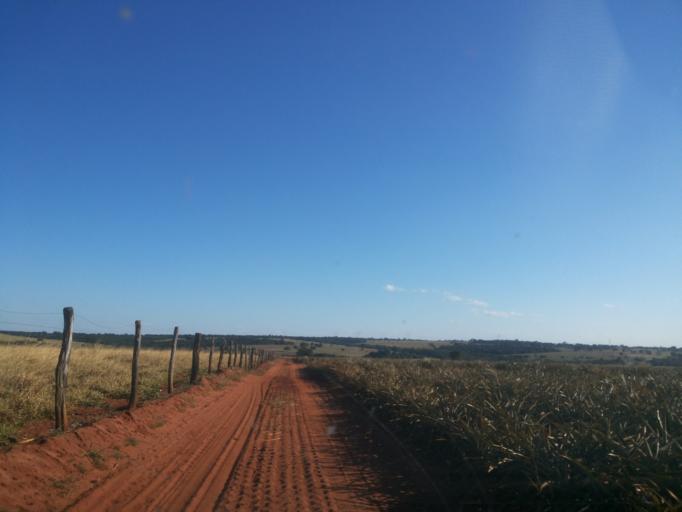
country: BR
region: Minas Gerais
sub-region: Centralina
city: Centralina
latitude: -18.7533
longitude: -49.0985
